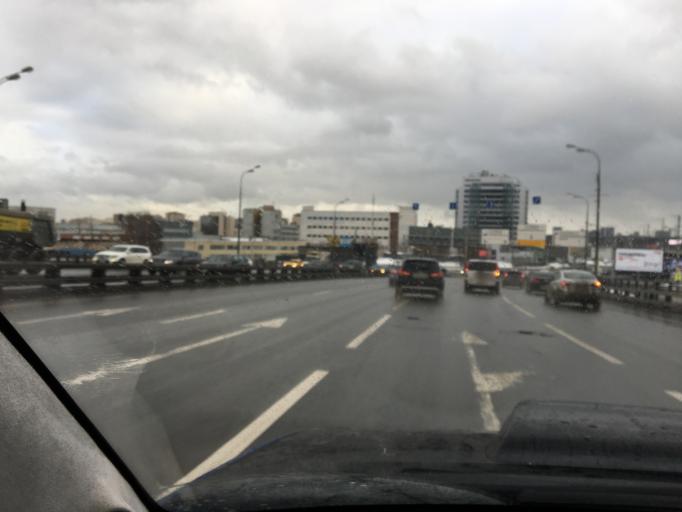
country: RU
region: Moskovskaya
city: Presnenskiy
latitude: 55.7352
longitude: 37.5414
